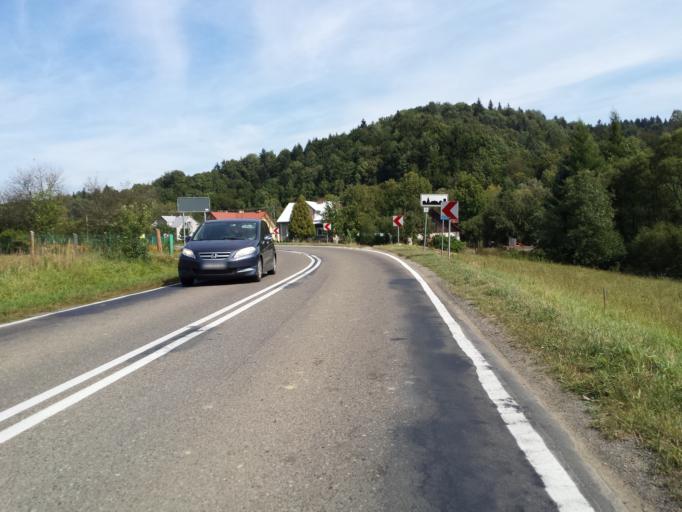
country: PL
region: Subcarpathian Voivodeship
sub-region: Powiat leski
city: Baligrod
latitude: 49.3869
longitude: 22.2876
